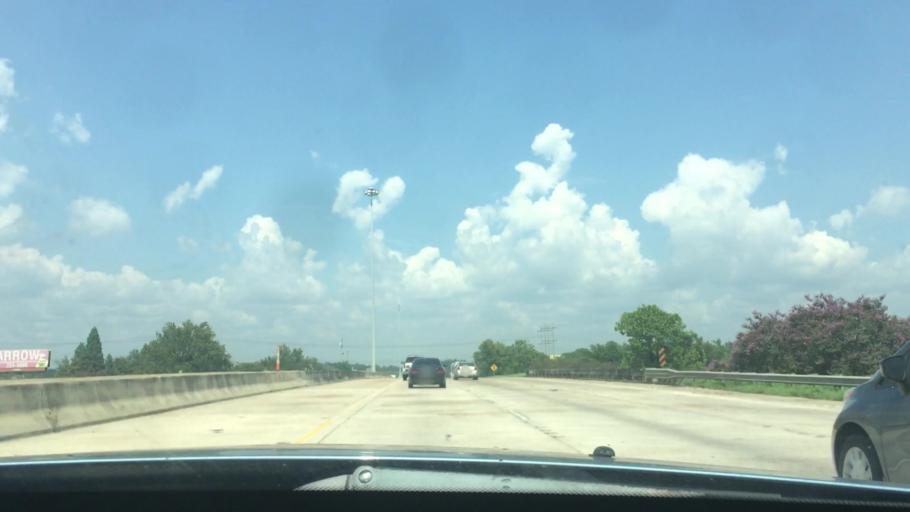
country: US
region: Louisiana
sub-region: East Baton Rouge Parish
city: Westminster
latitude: 30.4299
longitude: -91.0573
